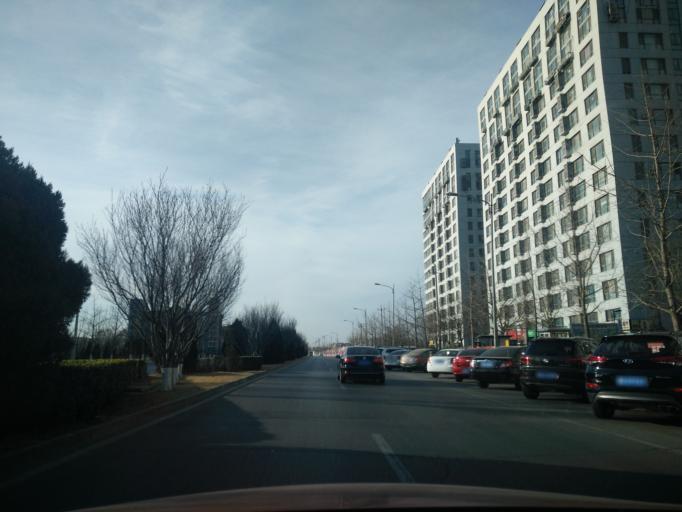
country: CN
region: Beijing
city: Jiugong
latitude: 39.7703
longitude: 116.4947
